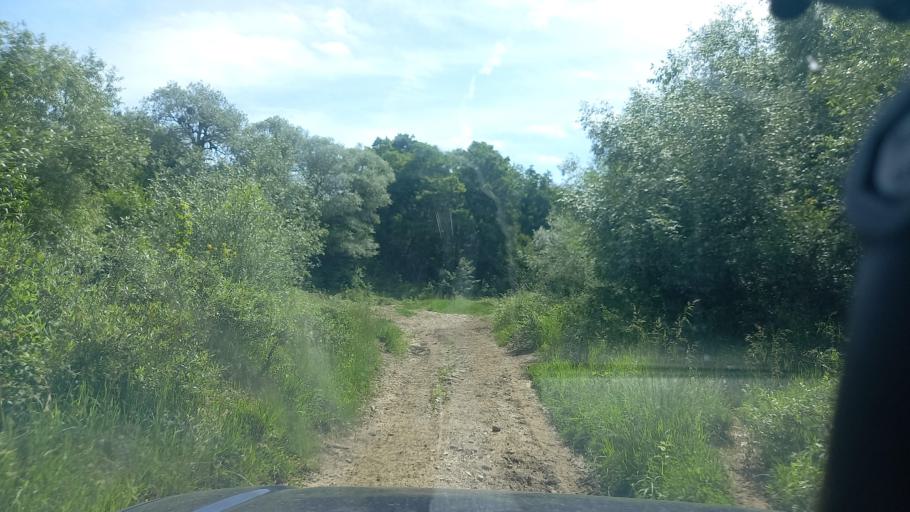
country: RU
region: Karachayevo-Cherkesiya
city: Kurdzhinovo
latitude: 44.1400
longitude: 41.0686
